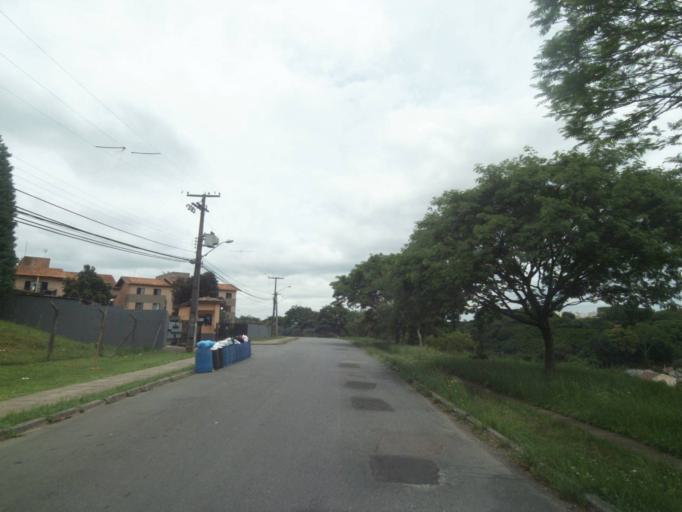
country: BR
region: Parana
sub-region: Curitiba
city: Curitiba
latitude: -25.3878
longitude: -49.2910
